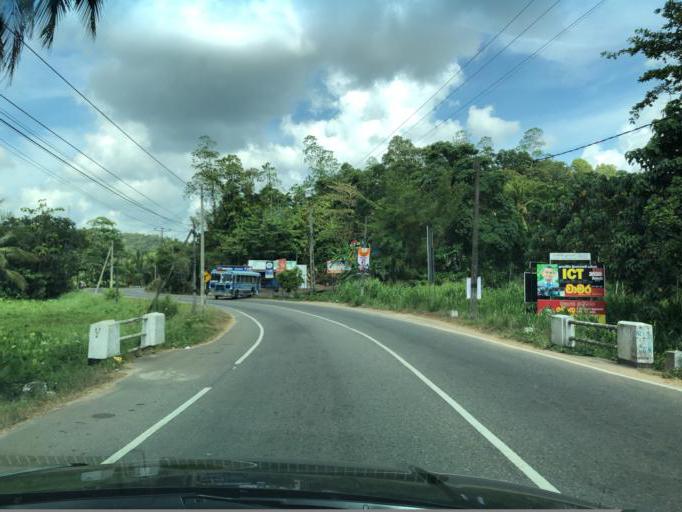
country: LK
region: Western
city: Horawala Junction
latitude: 6.5230
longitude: 80.1060
